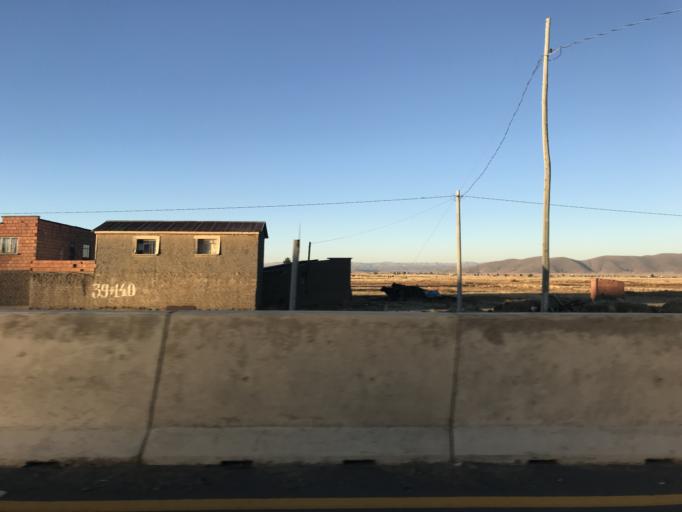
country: BO
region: La Paz
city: Batallas
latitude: -16.2994
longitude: -68.4976
